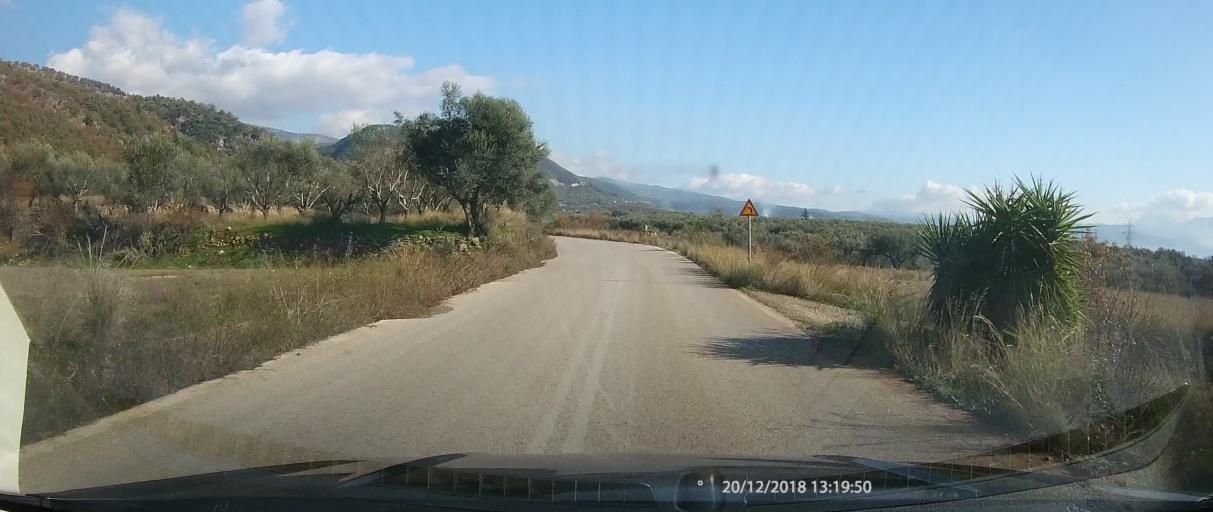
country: GR
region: West Greece
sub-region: Nomos Aitolias kai Akarnanias
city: Paravola
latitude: 38.6140
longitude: 21.5386
